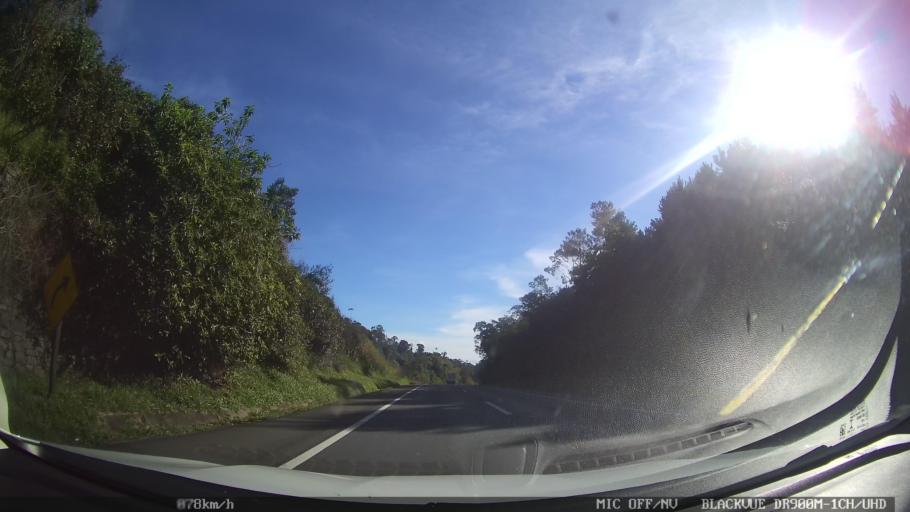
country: BR
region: Parana
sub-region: Antonina
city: Antonina
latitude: -25.0362
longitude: -48.5397
